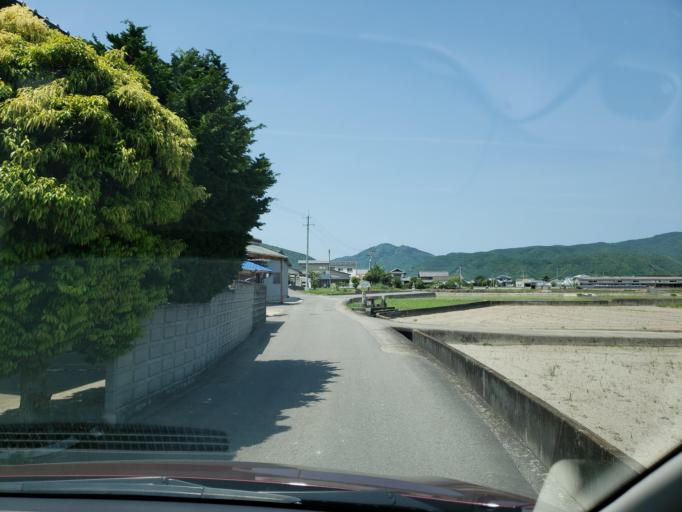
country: JP
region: Tokushima
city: Kamojimacho-jogejima
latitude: 34.0873
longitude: 134.2680
